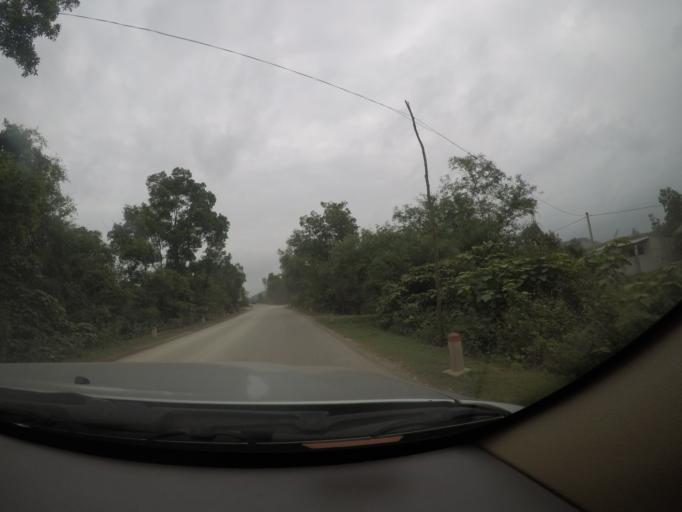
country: VN
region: Quang Binh
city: Quan Hau
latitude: 17.2879
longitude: 106.6462
